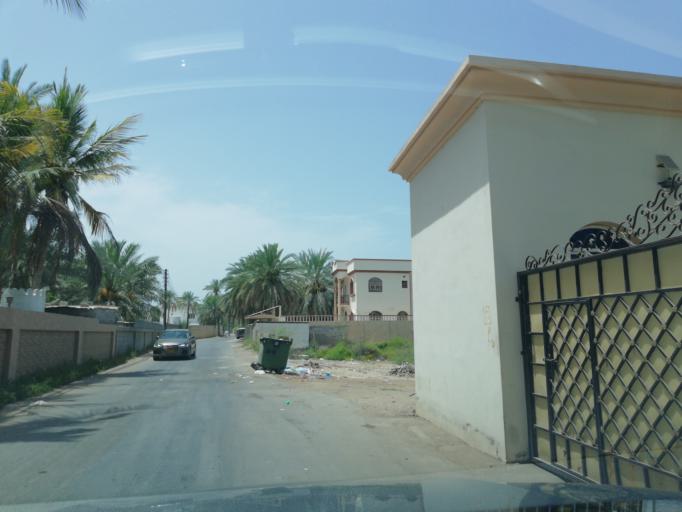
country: OM
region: Muhafazat Masqat
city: As Sib al Jadidah
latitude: 23.6600
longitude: 58.2104
